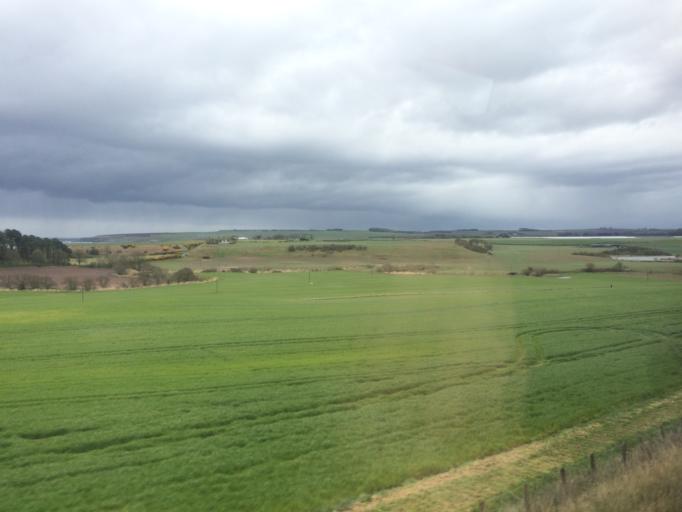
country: GB
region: Scotland
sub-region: Angus
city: Montrose
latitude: 56.6550
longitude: -2.5194
